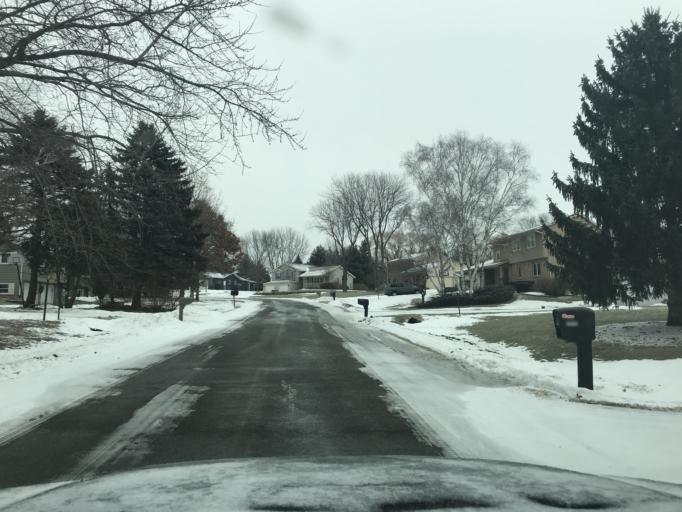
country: US
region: Wisconsin
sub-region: Dane County
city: Cottage Grove
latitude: 43.0938
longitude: -89.2326
